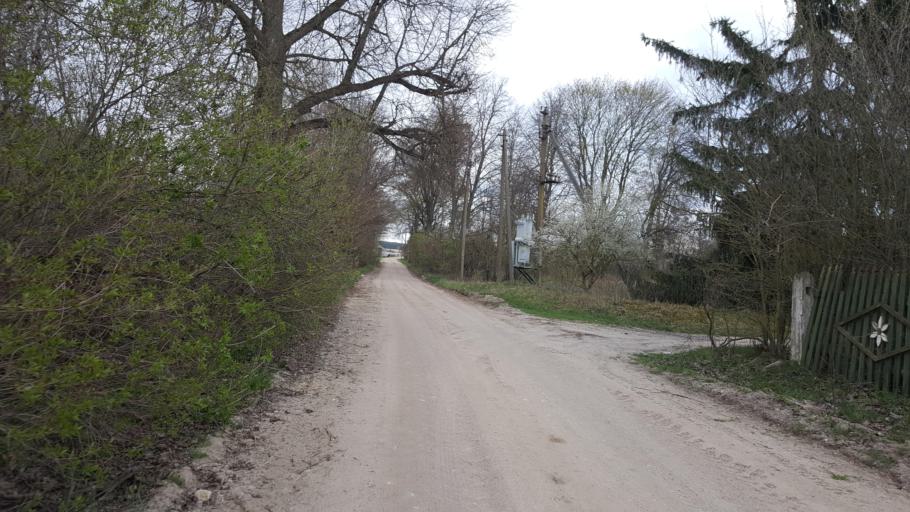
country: BY
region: Brest
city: Kamyanyets
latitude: 52.4066
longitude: 23.7134
